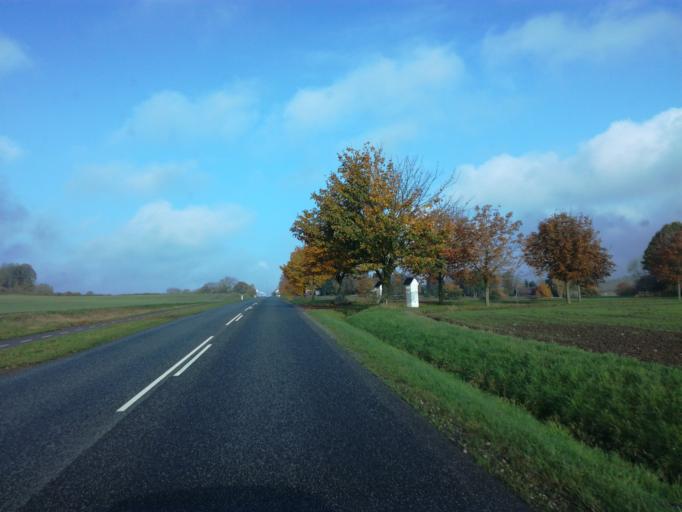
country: DK
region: South Denmark
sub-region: Vejle Kommune
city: Borkop
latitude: 55.6602
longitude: 9.6315
